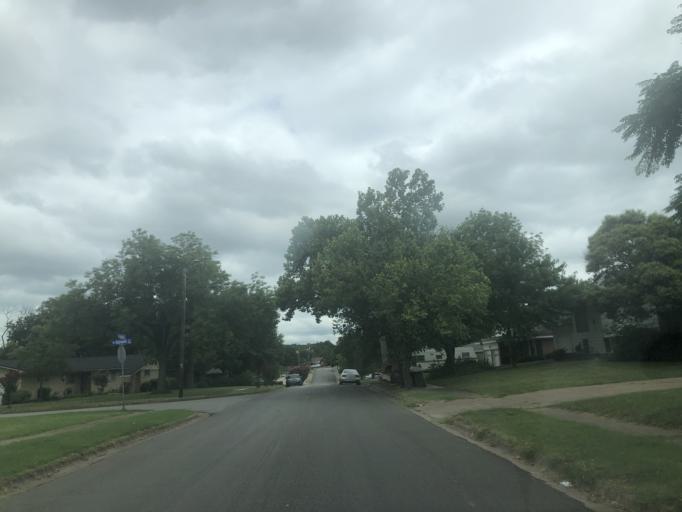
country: US
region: Texas
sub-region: Dallas County
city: Duncanville
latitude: 32.6405
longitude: -96.9056
